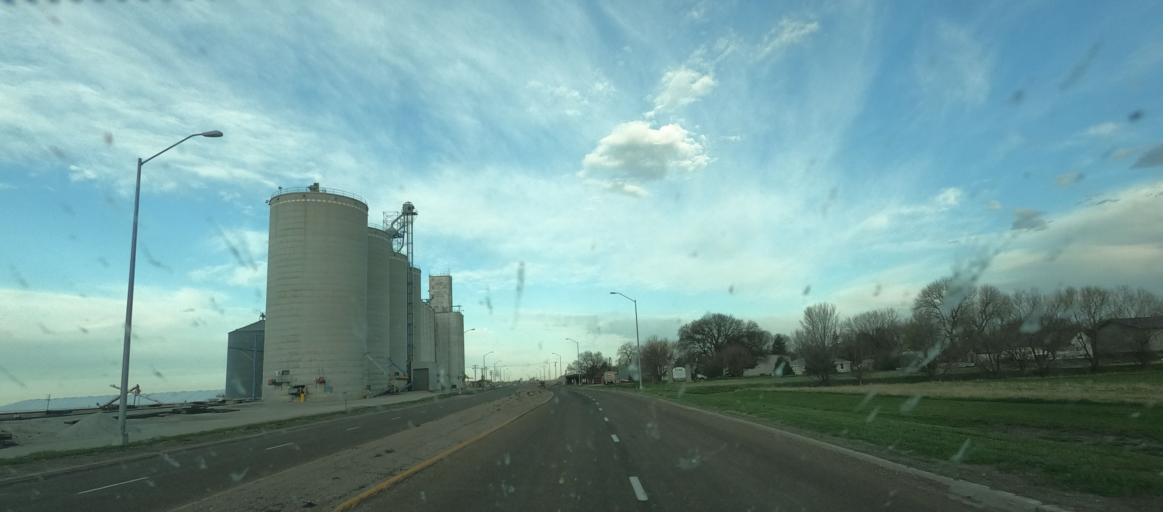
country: US
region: Nebraska
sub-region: Phelps County
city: Holdrege
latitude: 40.4613
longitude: -99.2471
